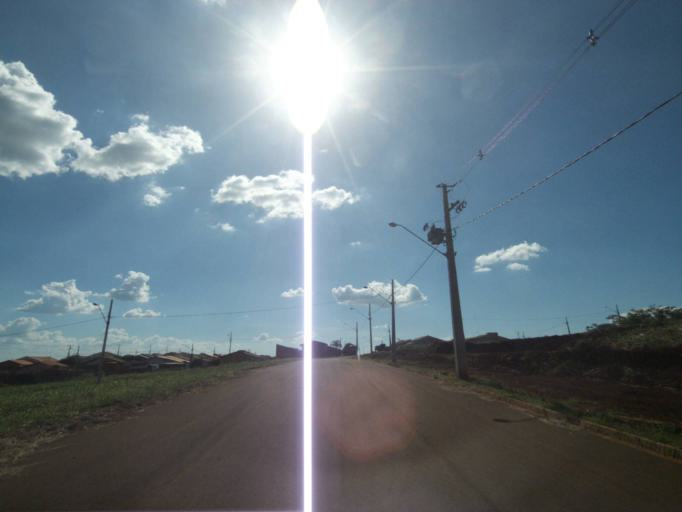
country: BR
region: Parana
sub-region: Sertanopolis
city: Sertanopolis
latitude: -23.0444
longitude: -50.8154
